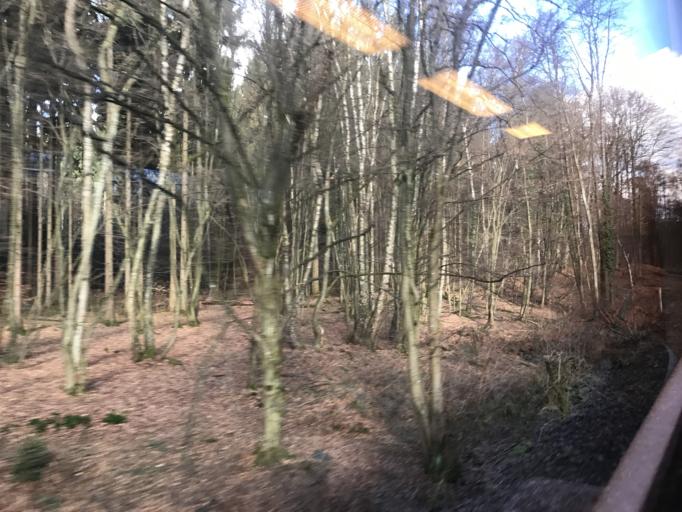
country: DE
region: Hesse
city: Kelkheim (Taunus)
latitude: 50.1610
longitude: 8.4444
